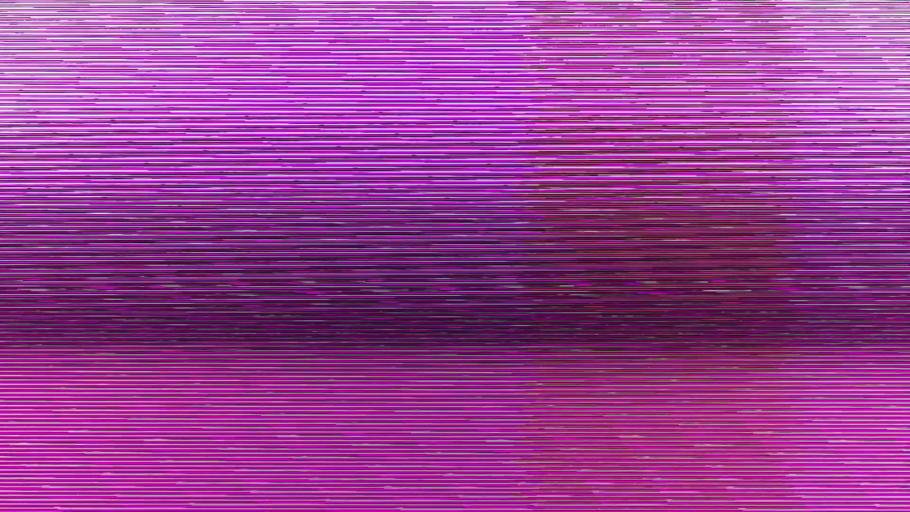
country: US
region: Michigan
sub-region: Wayne County
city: Canton
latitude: 42.3247
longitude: -83.4881
